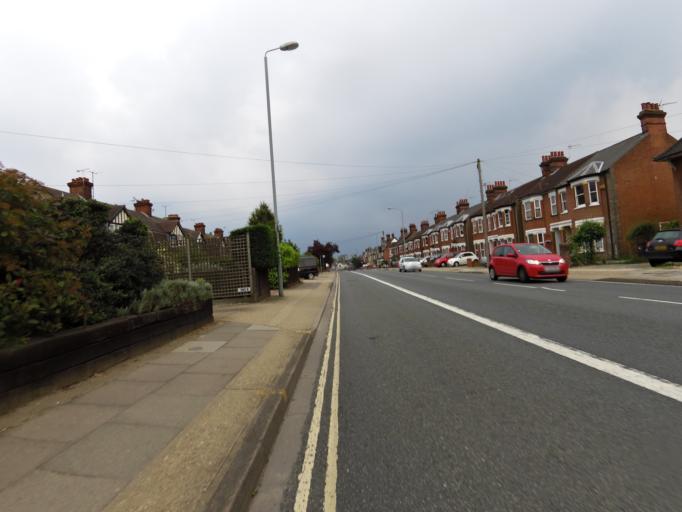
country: GB
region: England
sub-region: Suffolk
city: Ipswich
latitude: 52.0702
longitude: 1.1343
